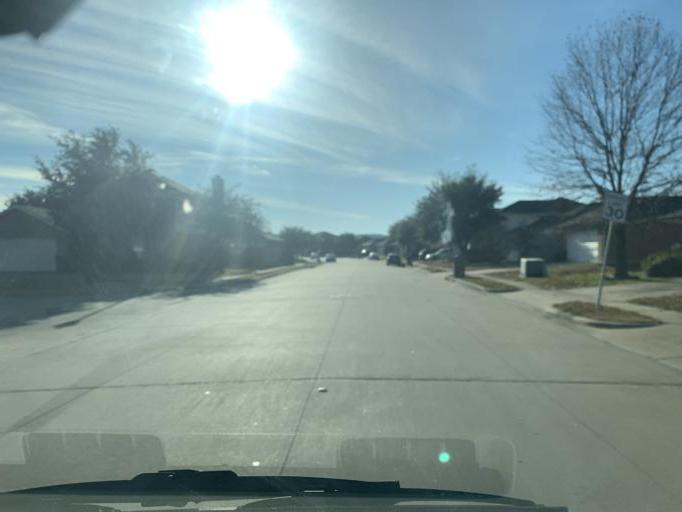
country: US
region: Texas
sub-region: Dallas County
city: Duncanville
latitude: 32.6566
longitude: -96.9780
